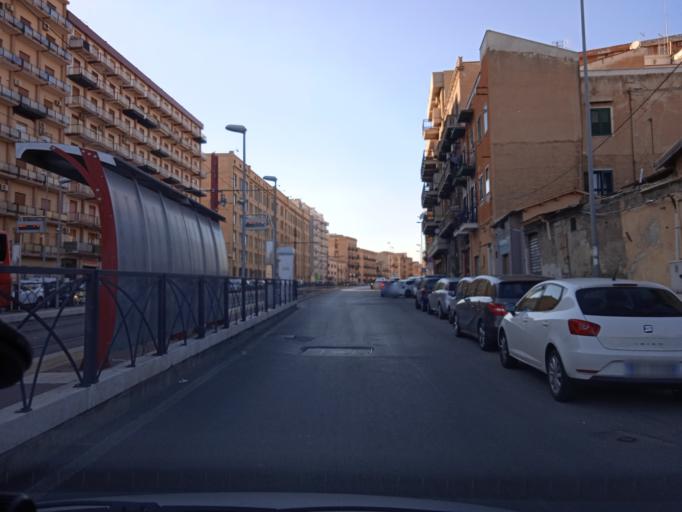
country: IT
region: Sicily
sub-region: Palermo
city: Palermo
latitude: 38.1070
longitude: 13.3732
